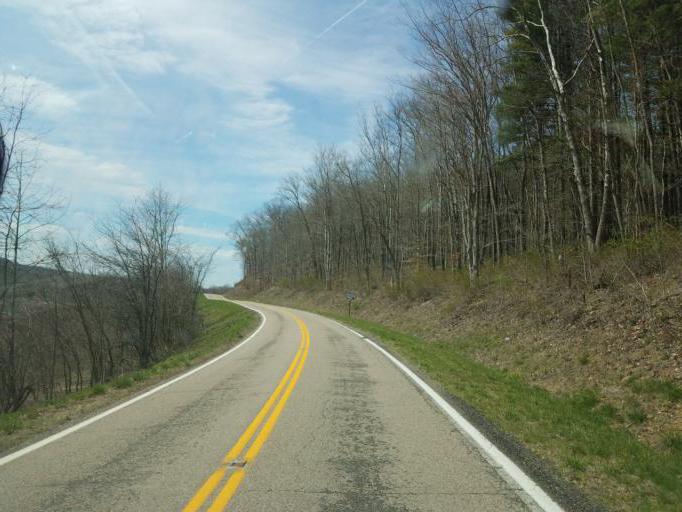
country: US
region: Ohio
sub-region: Knox County
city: Oak Hill
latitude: 40.3754
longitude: -82.1885
